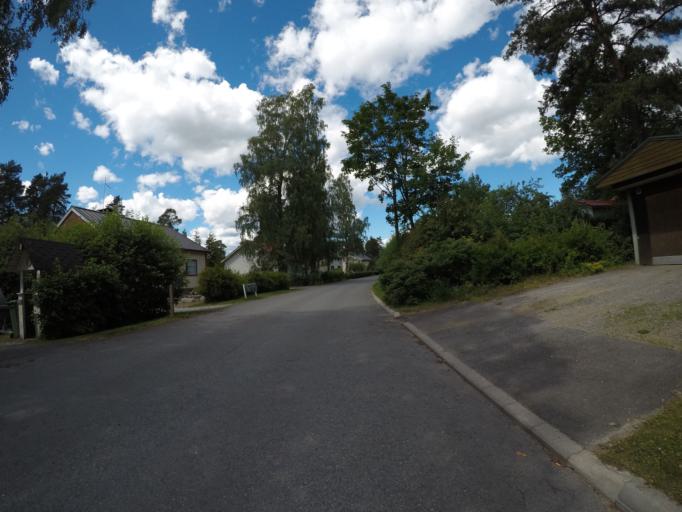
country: FI
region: Haeme
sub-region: Haemeenlinna
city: Haemeenlinna
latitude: 61.0163
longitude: 24.4284
